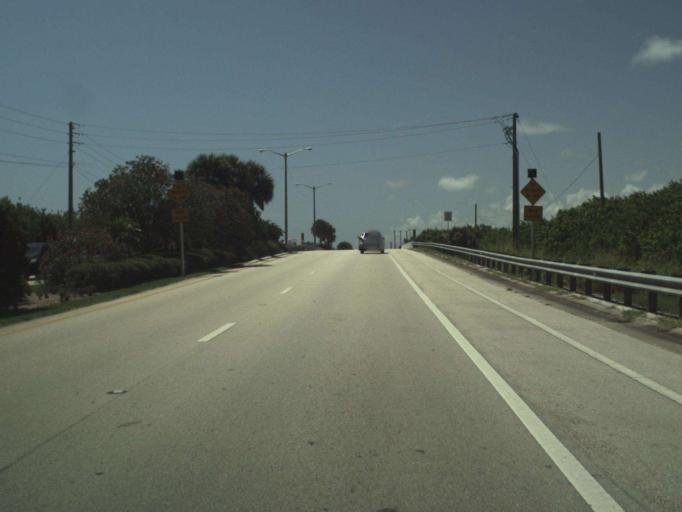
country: US
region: Florida
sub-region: Indian River County
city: Vero Beach
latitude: 27.6507
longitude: -80.3834
